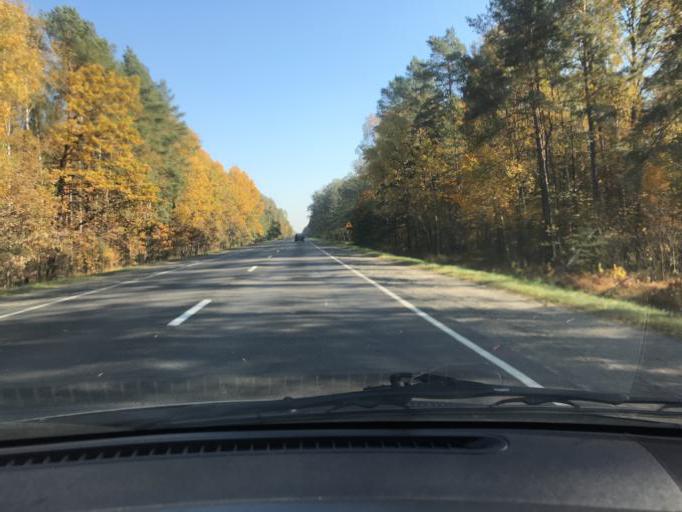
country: BY
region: Brest
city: Mikashevichy
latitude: 52.2429
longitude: 27.3365
